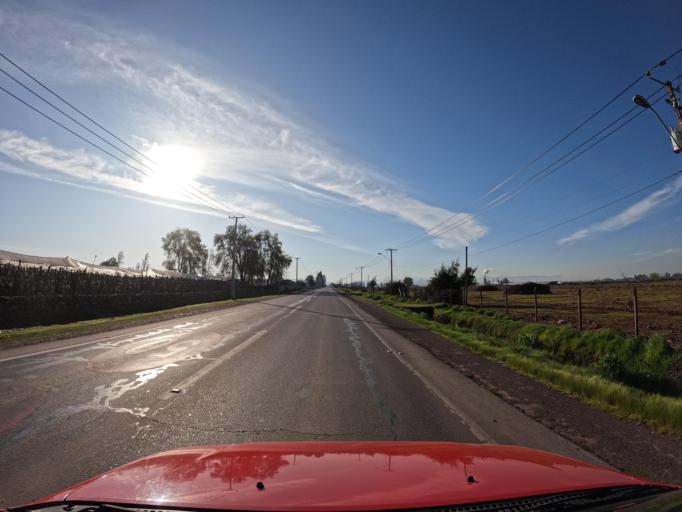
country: CL
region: Maule
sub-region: Provincia de Curico
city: Teno
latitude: -34.8695
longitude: -71.0878
